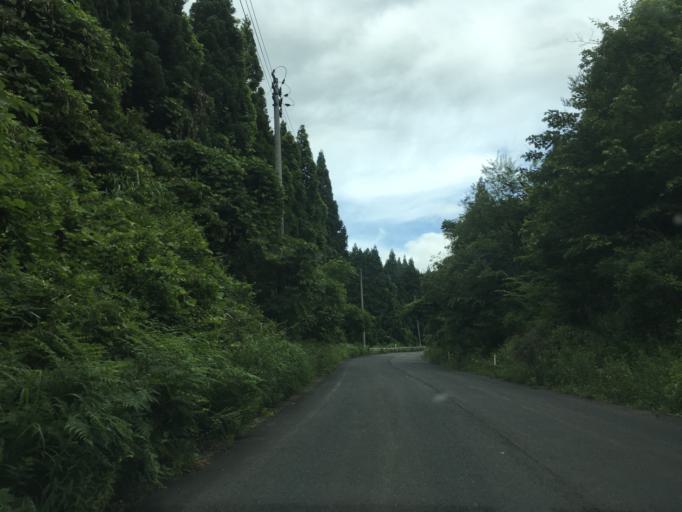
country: JP
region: Iwate
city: Ichinoseki
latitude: 38.8723
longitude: 141.3950
